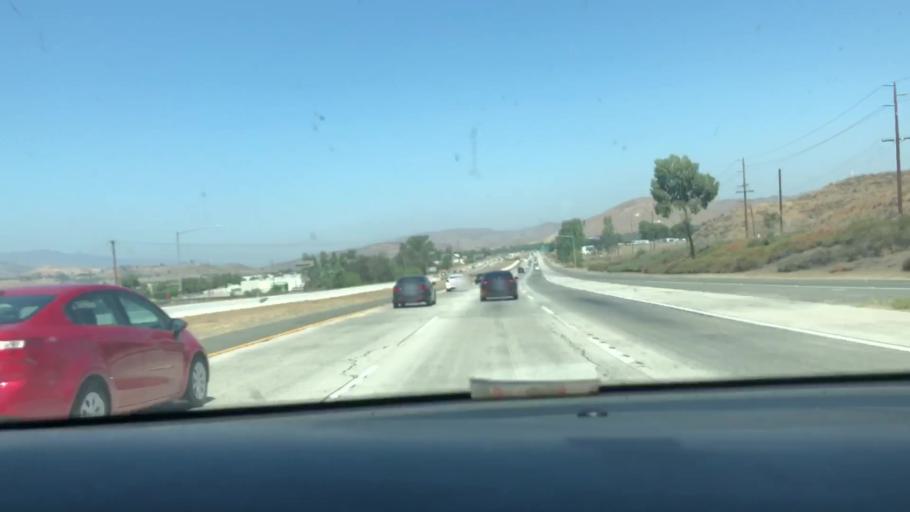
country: US
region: California
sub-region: Riverside County
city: Lake Elsinore
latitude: 33.6791
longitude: -117.3255
